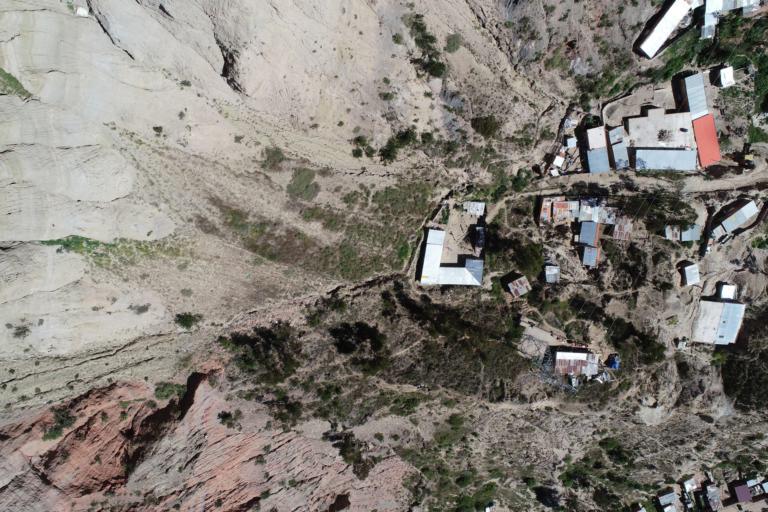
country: BO
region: La Paz
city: La Paz
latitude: -16.5273
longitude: -68.0921
